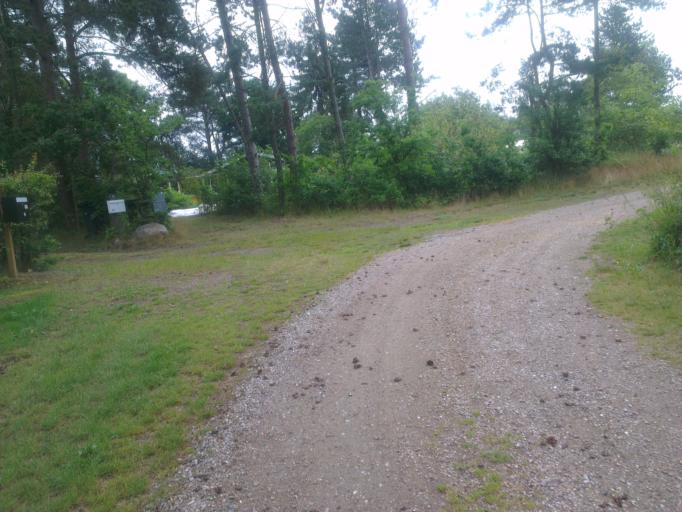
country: DK
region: Capital Region
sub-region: Frederikssund Kommune
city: Jaegerspris
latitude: 55.9061
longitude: 11.9289
